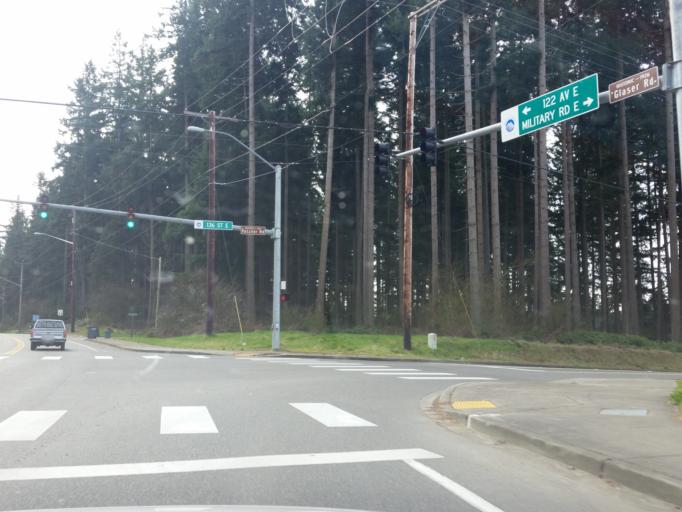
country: US
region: Washington
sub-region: Pierce County
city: South Hill
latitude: 47.1330
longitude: -122.2665
